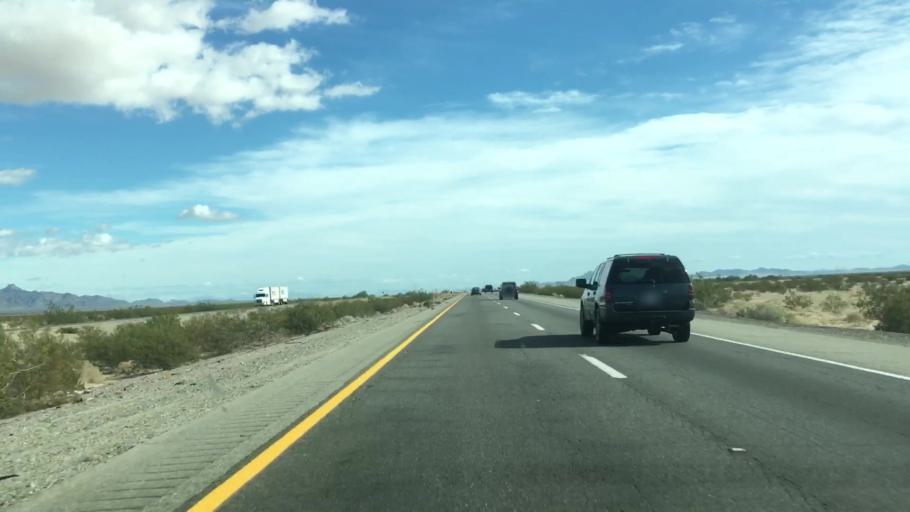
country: US
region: California
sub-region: Riverside County
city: Mesa Verde
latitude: 33.6225
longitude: -115.0428
